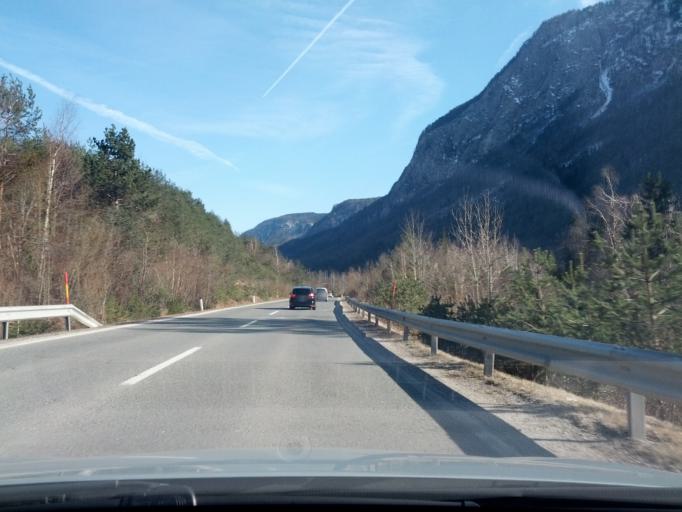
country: SI
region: Jesenice
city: Hrusica
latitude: 46.4552
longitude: 13.9860
